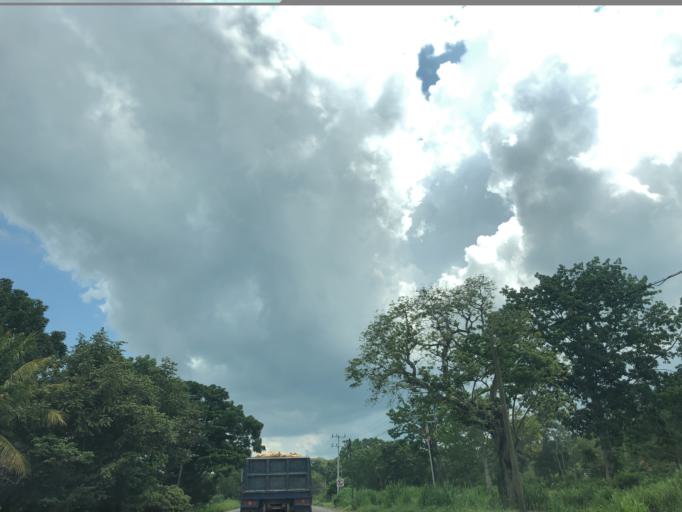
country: MX
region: Tabasco
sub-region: Comalcalco
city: Oriente 6ta. Seccion (Los Mulatos)
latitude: 18.1715
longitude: -93.2427
